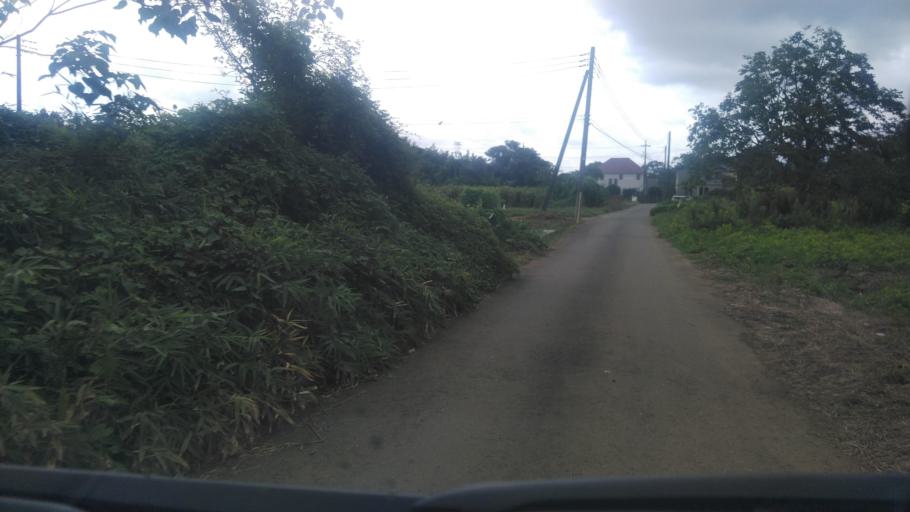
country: JP
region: Ibaraki
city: Naka
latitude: 36.0146
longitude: 140.1352
